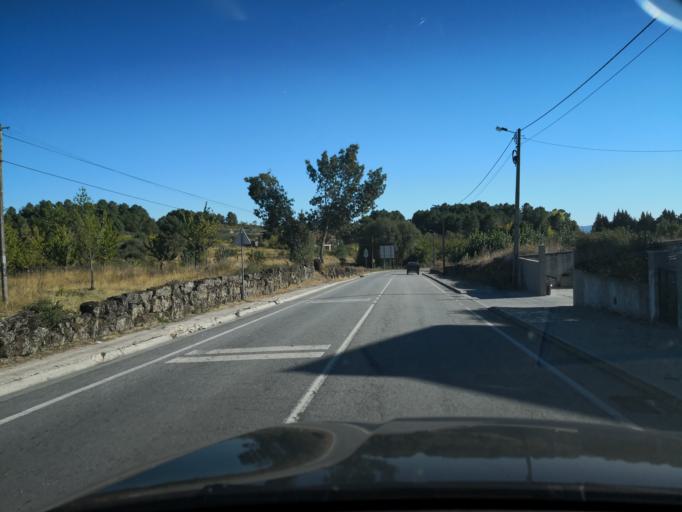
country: PT
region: Vila Real
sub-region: Valpacos
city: Valpacos
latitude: 41.6537
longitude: -7.3192
